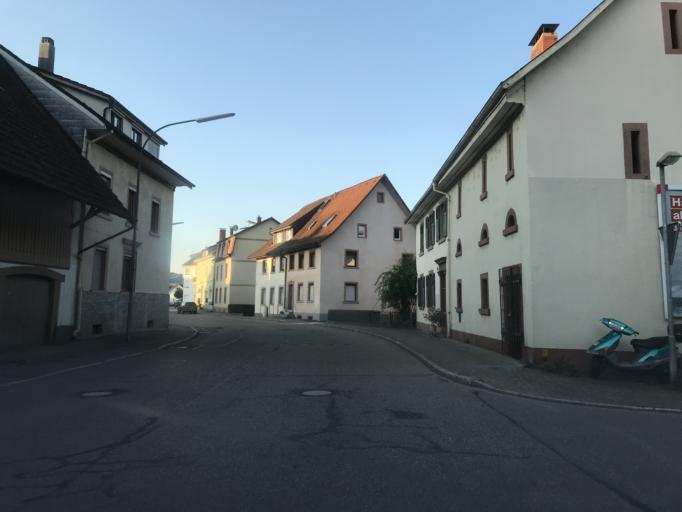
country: DE
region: Baden-Wuerttemberg
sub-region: Freiburg Region
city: Schopfheim
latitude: 47.6601
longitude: 7.8341
